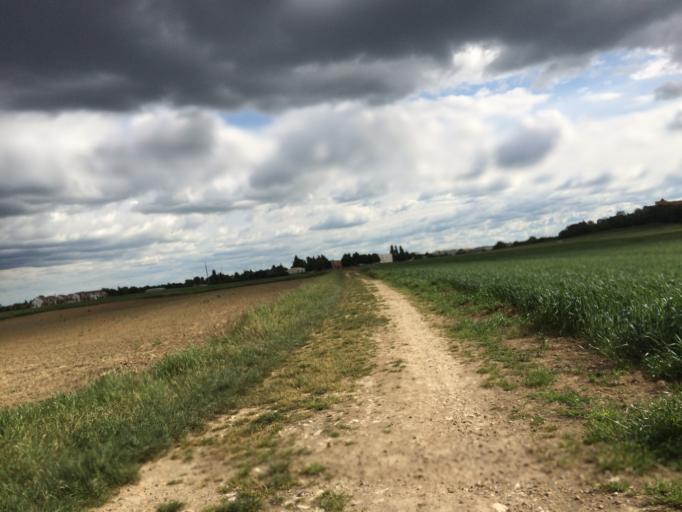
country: FR
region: Ile-de-France
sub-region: Departement de l'Essonne
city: Le Plessis-Pate
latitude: 48.6185
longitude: 2.3155
